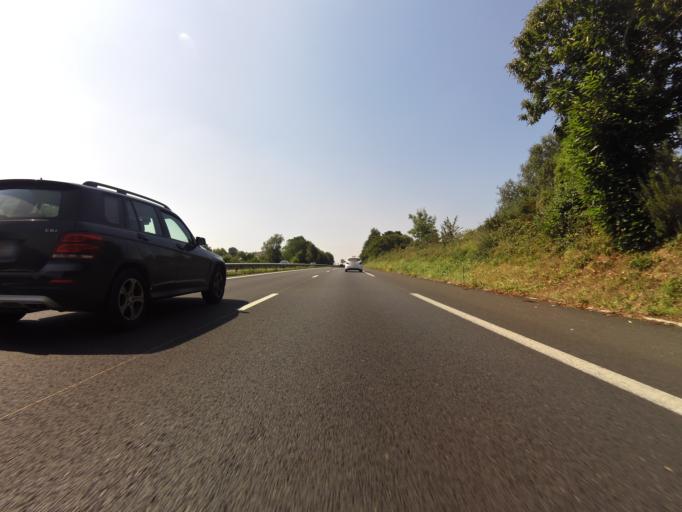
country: FR
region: Brittany
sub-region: Departement du Finistere
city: Plomelin
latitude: 47.9740
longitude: -4.1381
